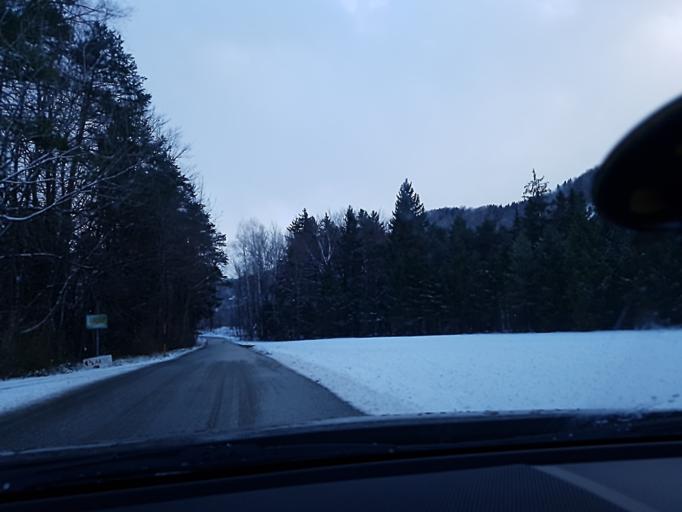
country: AT
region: Salzburg
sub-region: Politischer Bezirk Salzburg-Umgebung
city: Grodig
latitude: 47.7226
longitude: 13.0550
